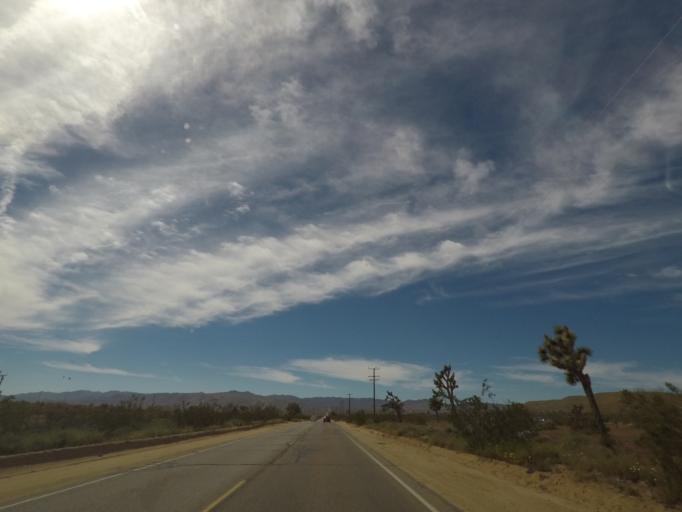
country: US
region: California
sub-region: San Bernardino County
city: Joshua Tree
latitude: 34.1722
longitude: -116.3696
